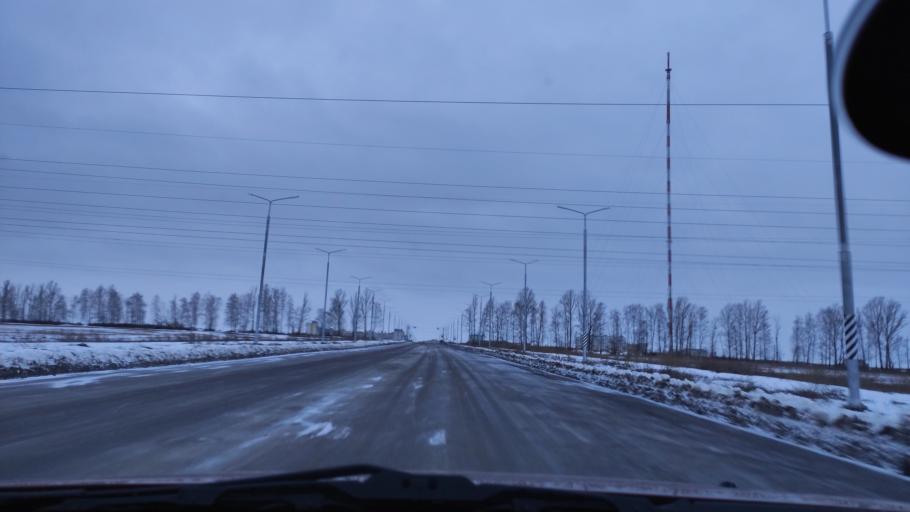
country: RU
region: Tambov
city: Donskoye
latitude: 52.7822
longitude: 41.4262
